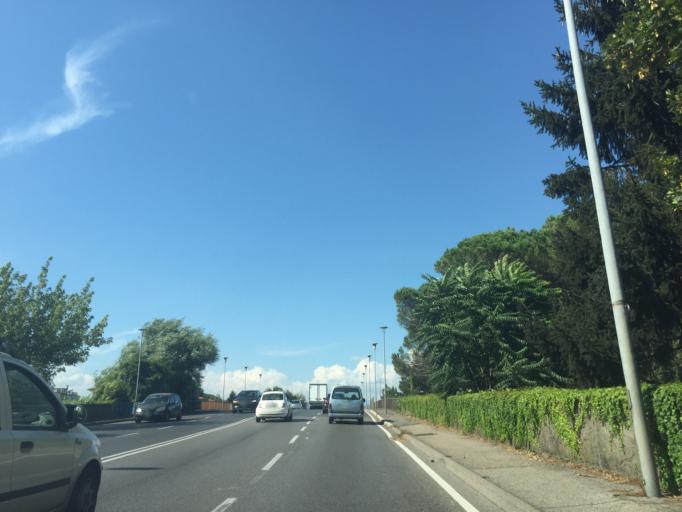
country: IT
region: Tuscany
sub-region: Provincia di Lucca
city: Lucca
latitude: 43.8369
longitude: 10.4950
